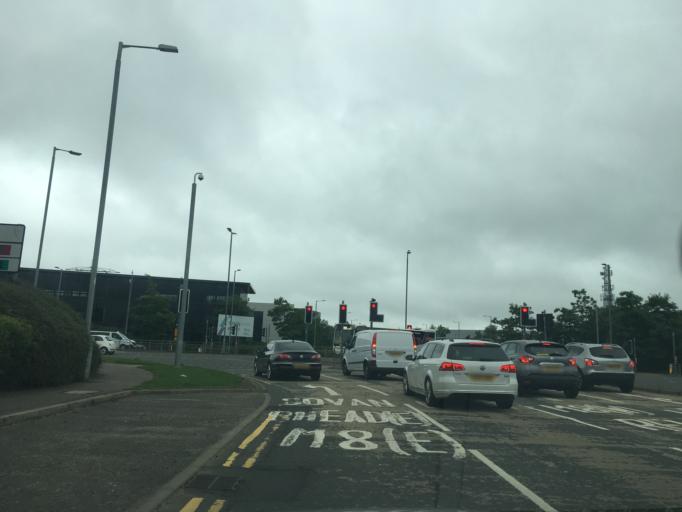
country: GB
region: Scotland
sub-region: Renfrewshire
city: Renfrew
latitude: 55.8740
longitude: -4.3682
